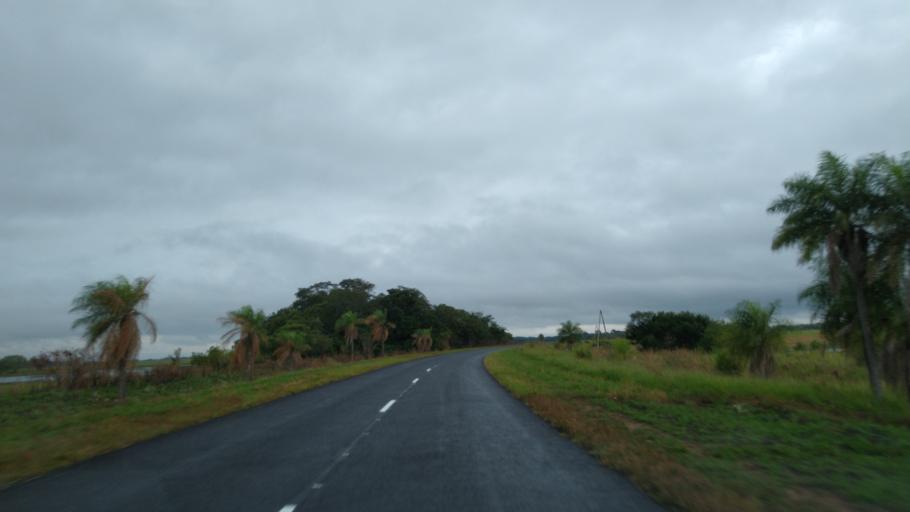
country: AR
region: Corrientes
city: Loreto
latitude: -27.6904
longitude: -57.2172
